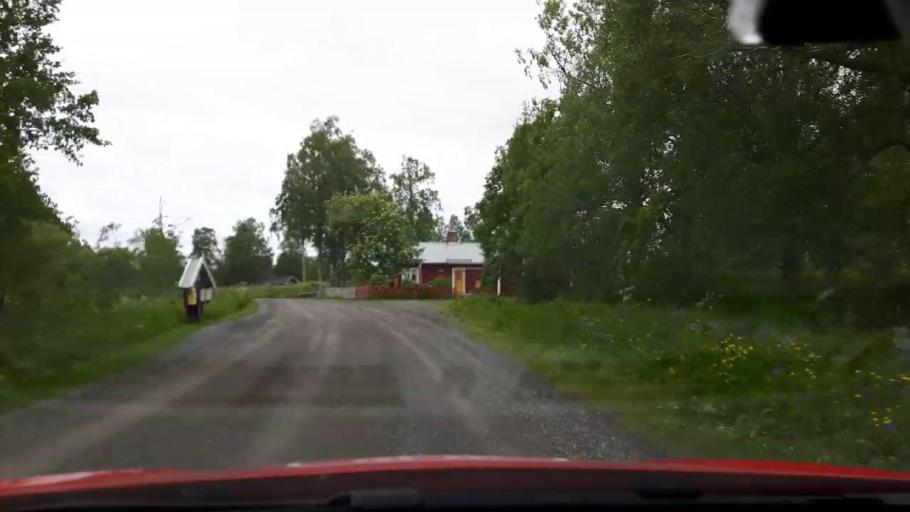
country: SE
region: Jaemtland
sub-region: Krokoms Kommun
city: Krokom
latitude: 63.2471
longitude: 14.5288
